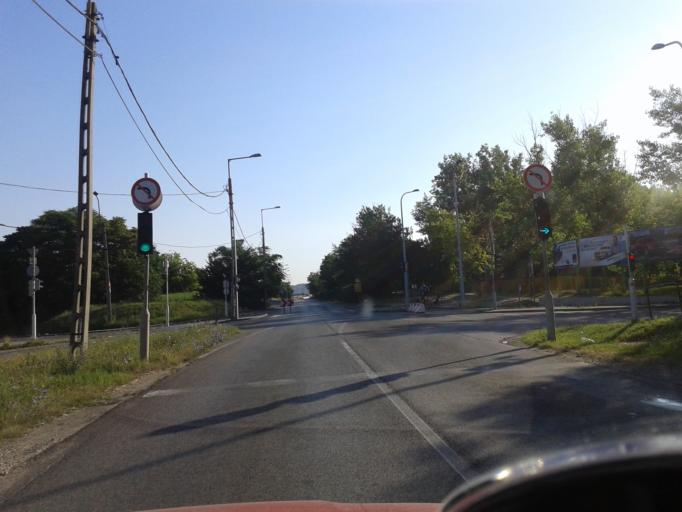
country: HU
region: Budapest
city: Budapest XI. keruelet
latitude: 47.4624
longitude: 19.0122
